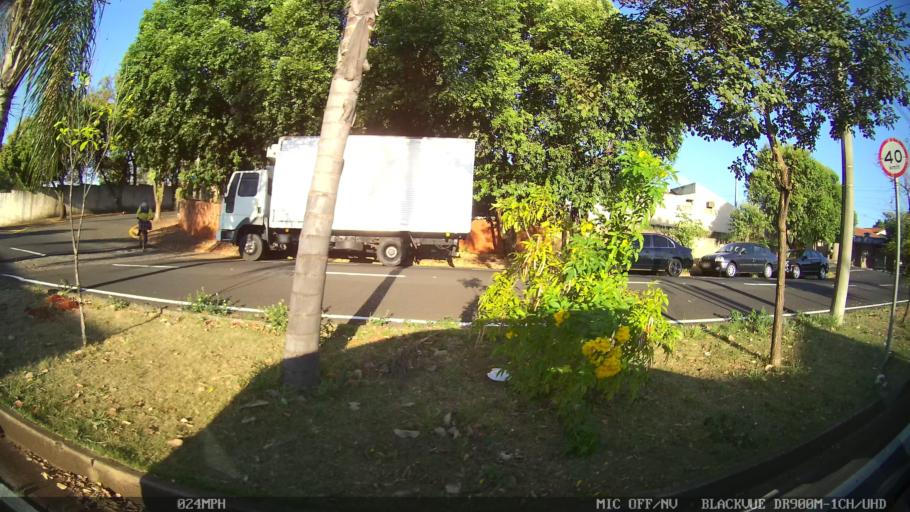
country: BR
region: Sao Paulo
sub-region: Sao Jose Do Rio Preto
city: Sao Jose do Rio Preto
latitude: -20.7895
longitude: -49.3476
